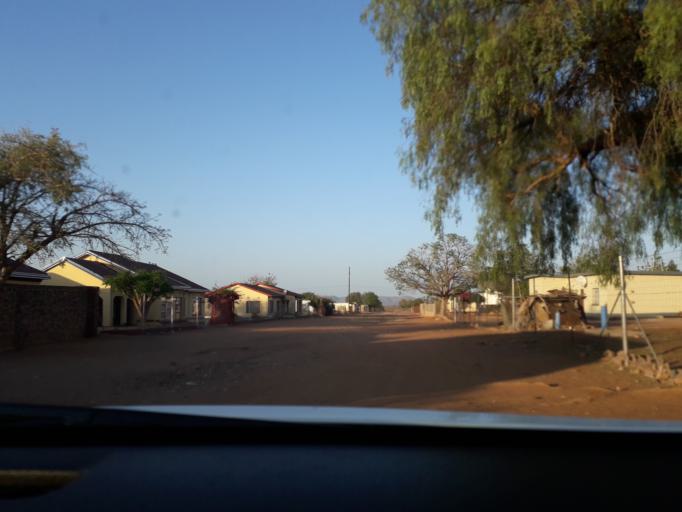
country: ZA
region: Limpopo
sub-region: Waterberg District Municipality
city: Mokopane
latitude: -23.9156
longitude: 28.8725
